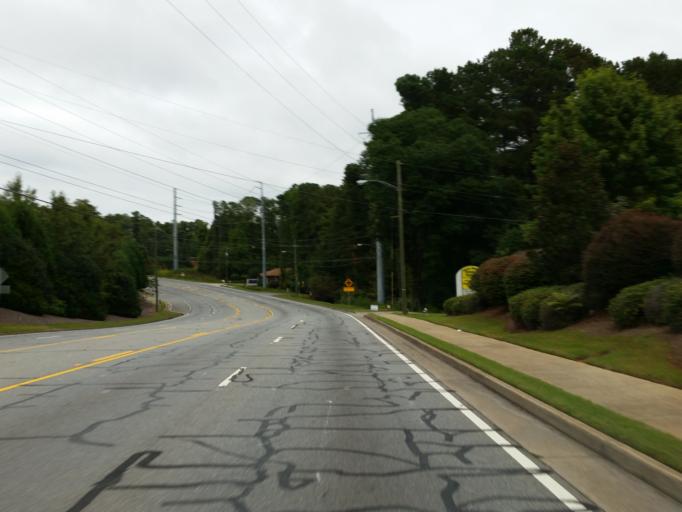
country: US
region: Georgia
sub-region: Cherokee County
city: Woodstock
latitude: 34.0545
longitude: -84.5234
